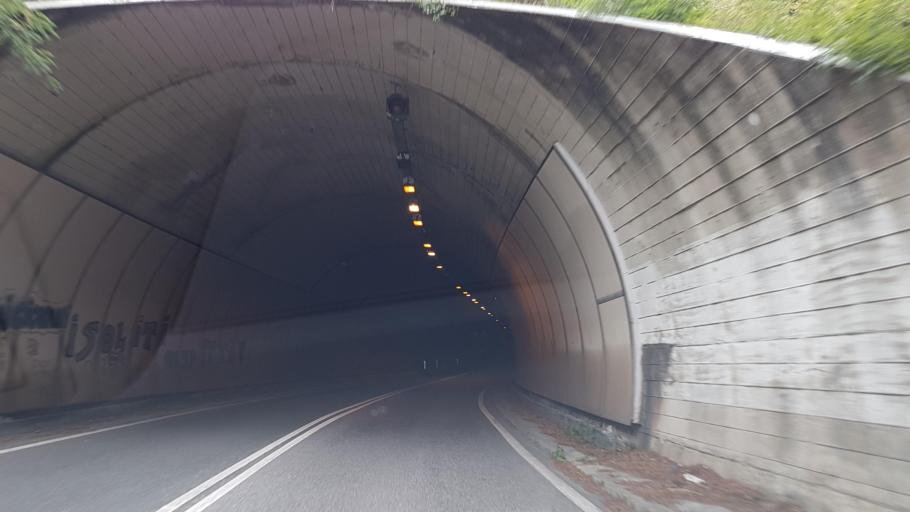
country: IT
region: Liguria
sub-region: Provincia di La Spezia
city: Levanto
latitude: 44.2015
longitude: 9.6226
